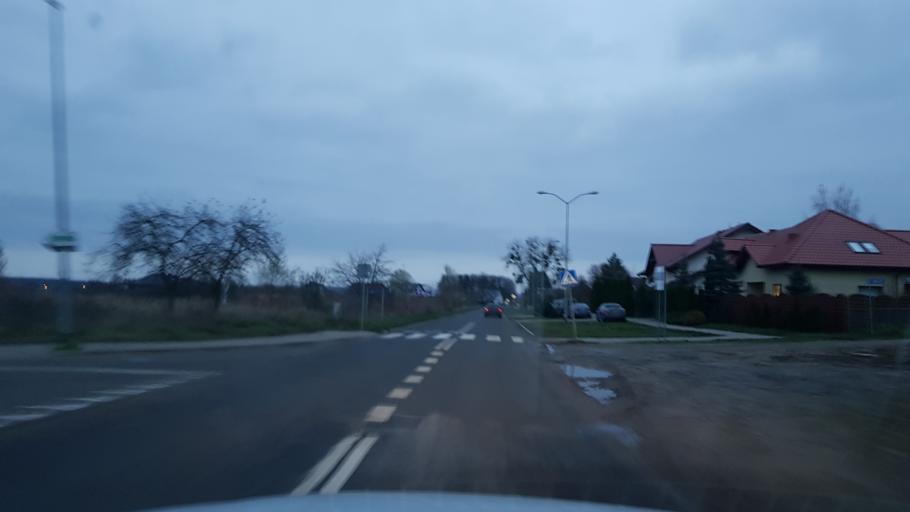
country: PL
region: West Pomeranian Voivodeship
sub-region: Powiat policki
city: Przeclaw
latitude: 53.4204
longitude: 14.4432
